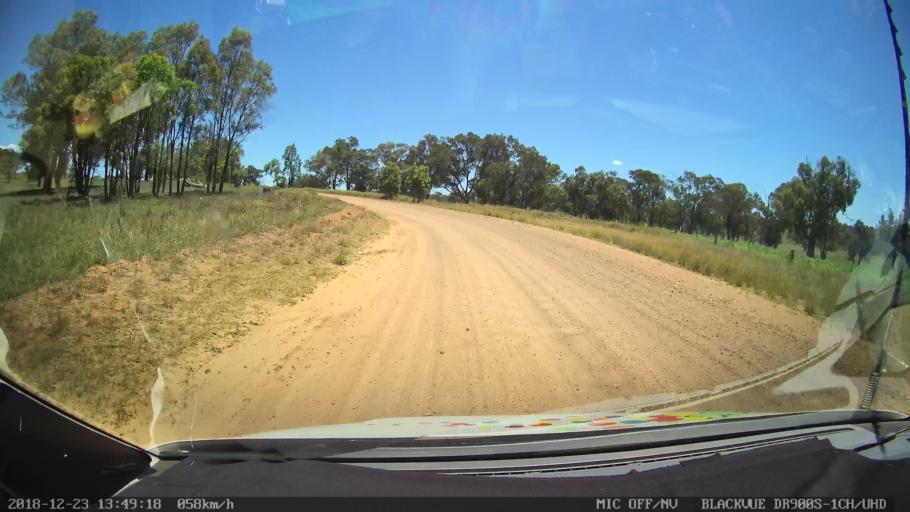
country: AU
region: New South Wales
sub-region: Tamworth Municipality
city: Manilla
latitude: -30.5207
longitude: 151.1090
